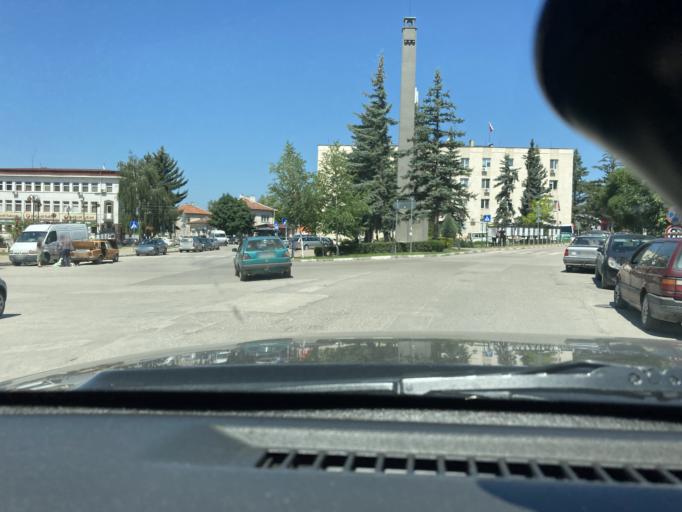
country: BG
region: Sofiya
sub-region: Obshtina Slivnitsa
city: Slivnitsa
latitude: 42.8519
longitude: 23.0387
